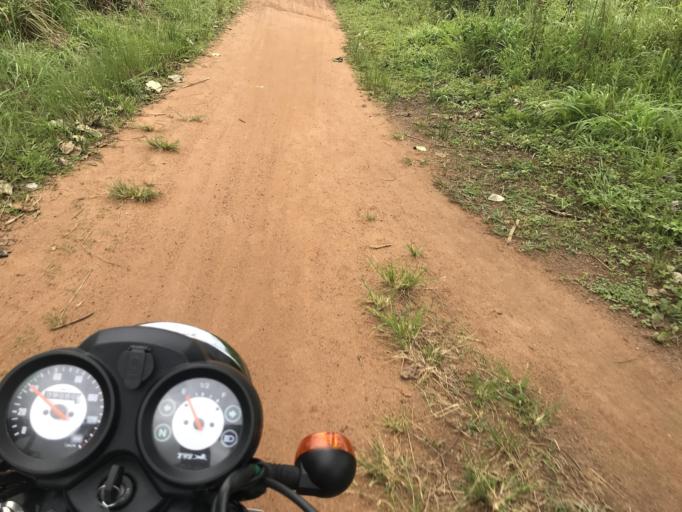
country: SL
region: Eastern Province
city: Buedu
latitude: 8.4752
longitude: -10.3165
